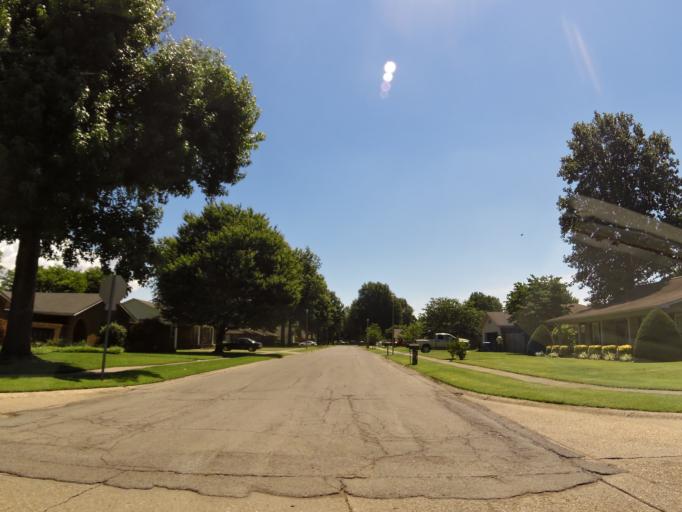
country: US
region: Missouri
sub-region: New Madrid County
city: New Madrid
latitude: 36.5985
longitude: -89.5266
